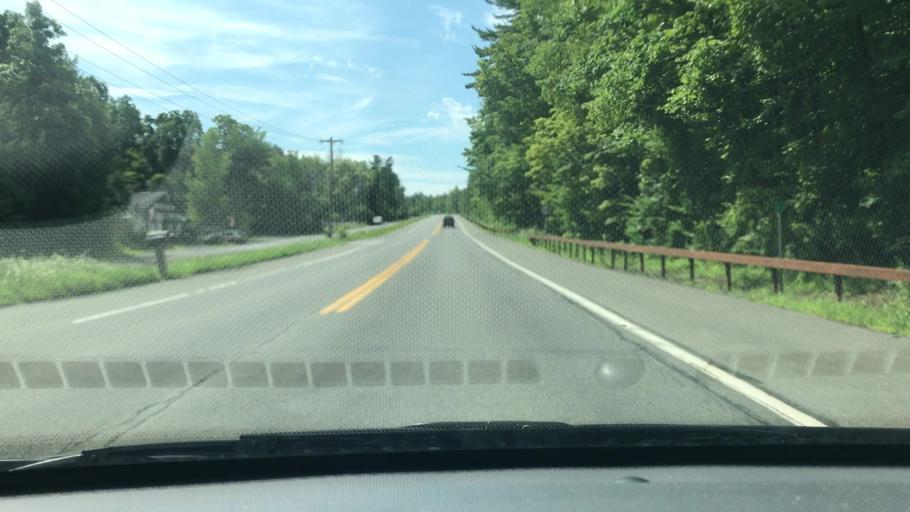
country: US
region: New York
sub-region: Ulster County
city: Shokan
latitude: 41.9993
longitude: -74.2646
